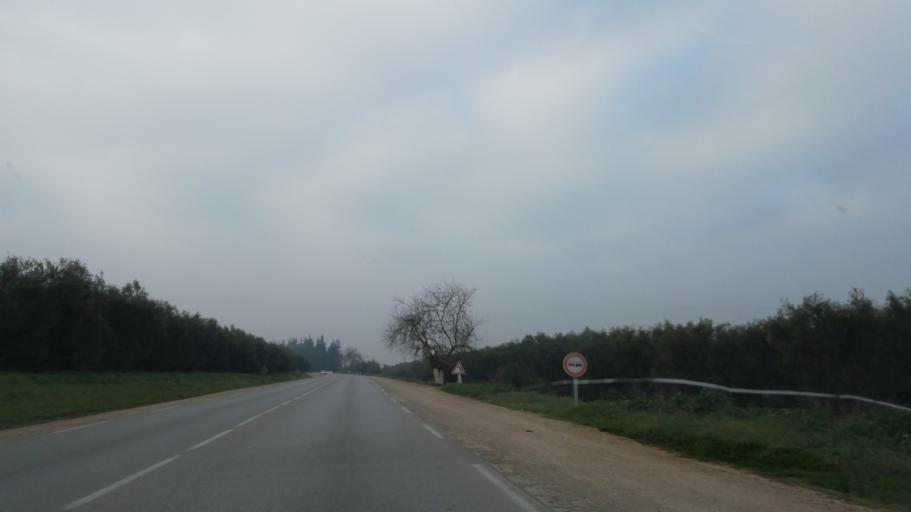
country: DZ
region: Relizane
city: Djidiouia
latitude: 35.9441
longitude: 0.8652
